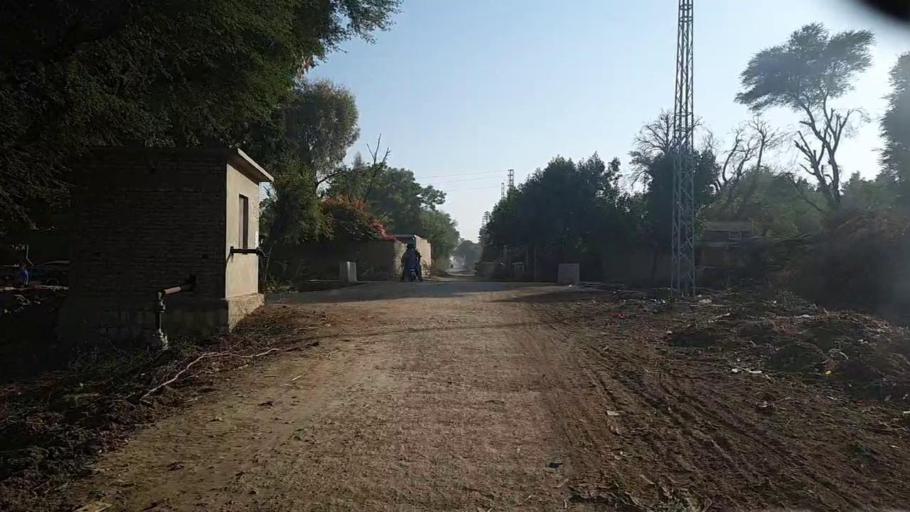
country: PK
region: Sindh
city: Darya Khan Marri
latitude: 26.6972
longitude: 68.3625
